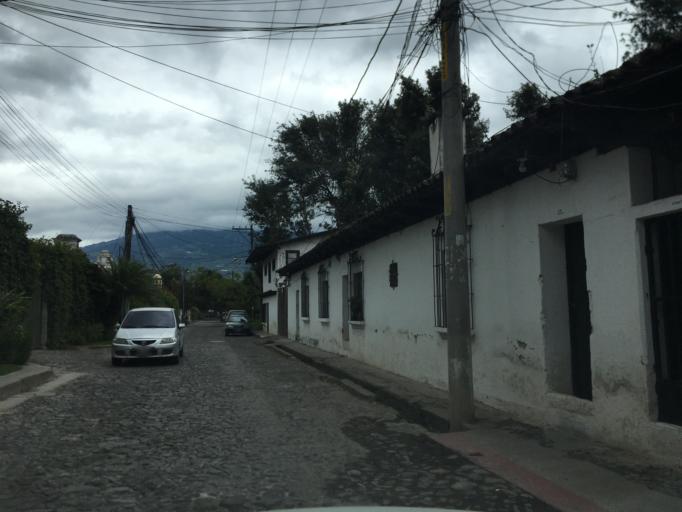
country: GT
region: Sacatepequez
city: Antigua Guatemala
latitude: 14.5516
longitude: -90.7343
